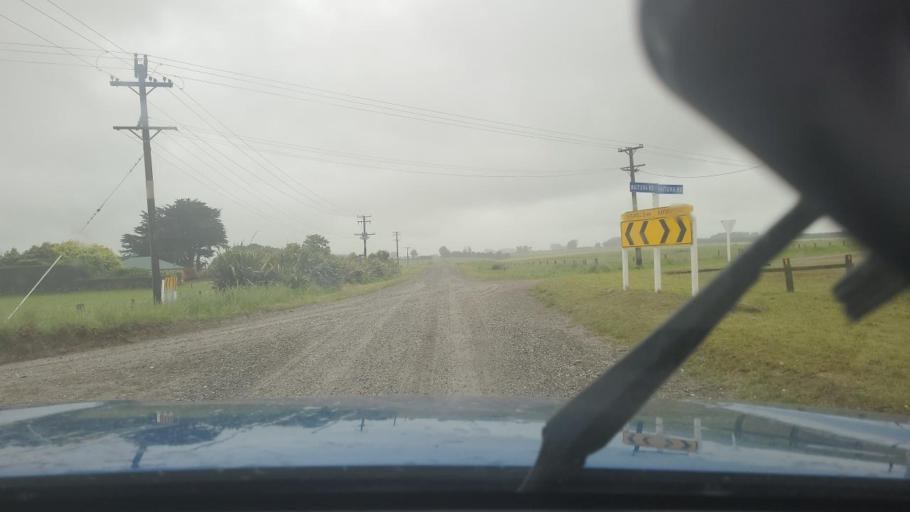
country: NZ
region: Southland
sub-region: Invercargill City
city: Invercargill
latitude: -46.4252
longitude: 168.6236
